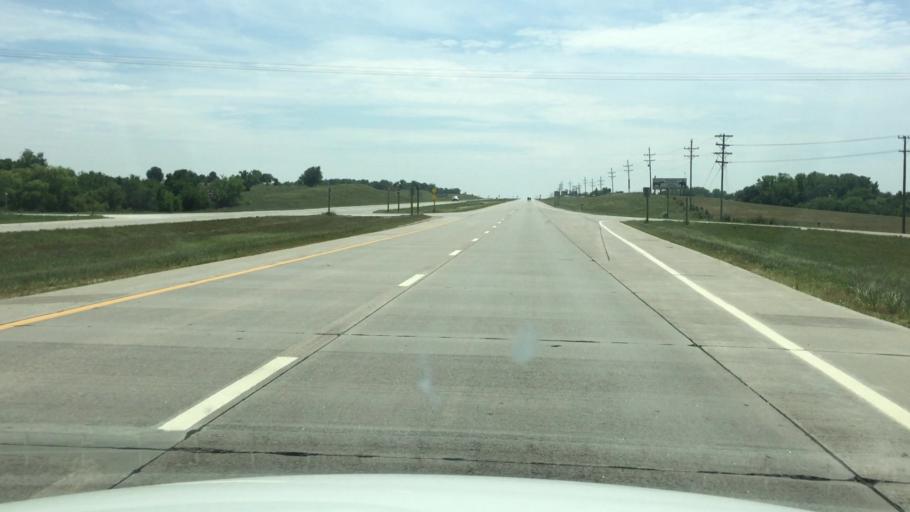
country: US
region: Kansas
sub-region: Jackson County
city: Holton
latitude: 39.3039
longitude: -95.7195
